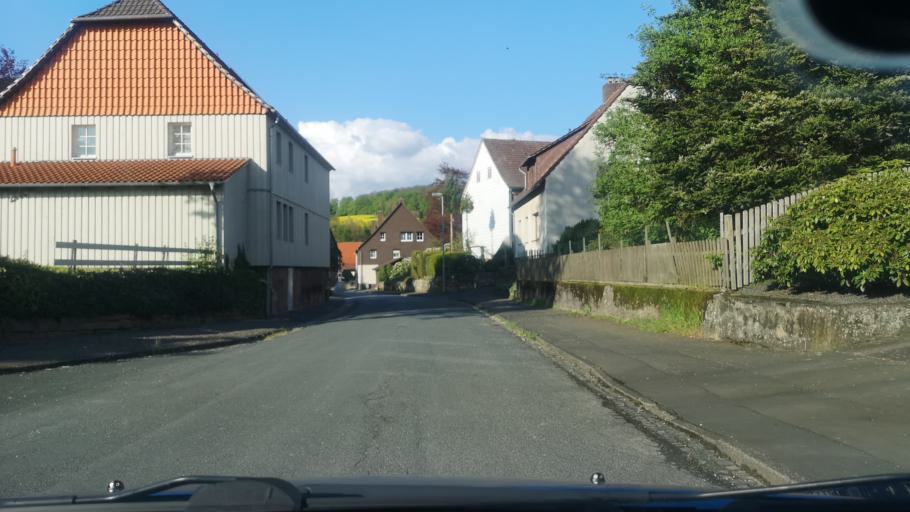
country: DE
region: Lower Saxony
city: Uslar
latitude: 51.6527
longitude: 9.6804
